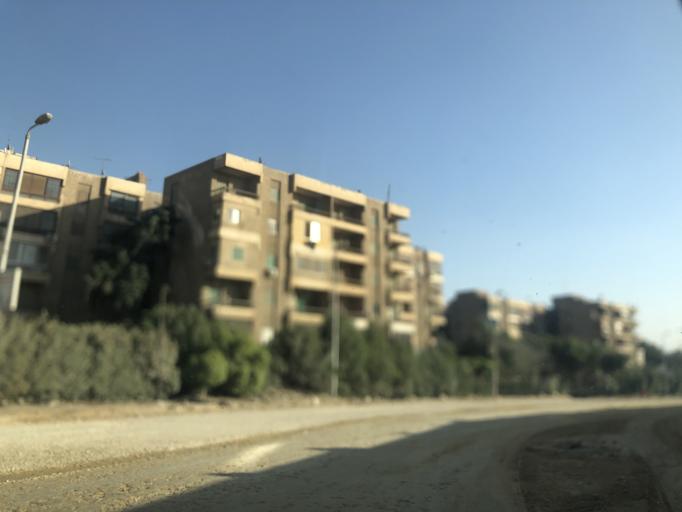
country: EG
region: Al Jizah
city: Al Jizah
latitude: 29.9858
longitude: 31.1125
